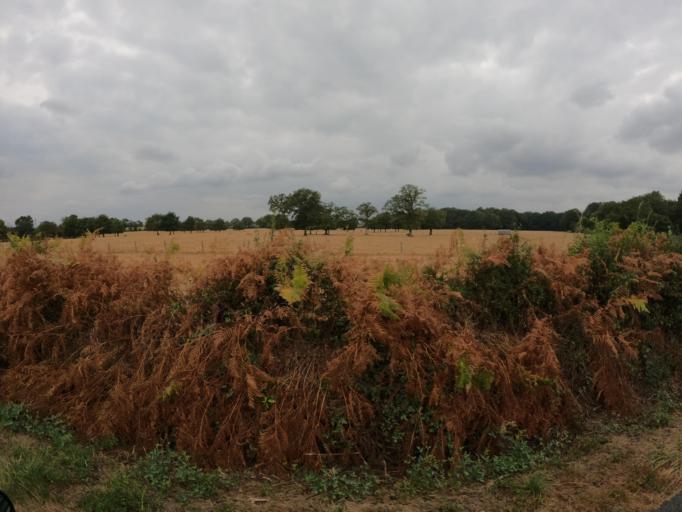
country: FR
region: Pays de la Loire
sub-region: Departement de Maine-et-Loire
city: La Romagne
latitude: 47.0416
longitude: -1.0359
